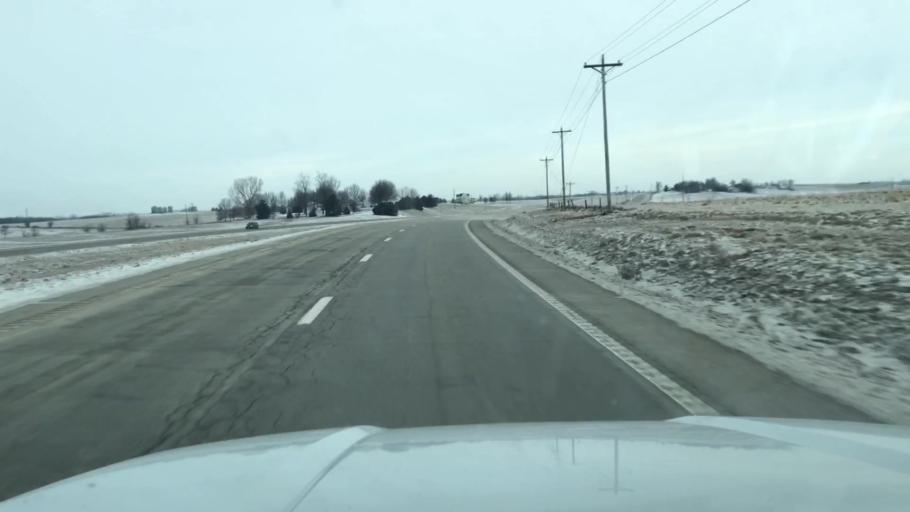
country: US
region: Missouri
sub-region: Andrew County
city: Savannah
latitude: 39.9834
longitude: -94.8796
